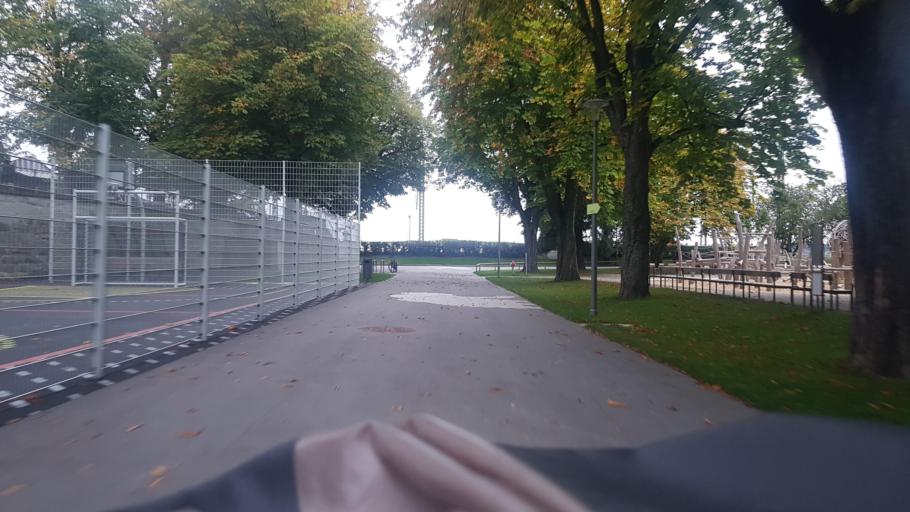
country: DE
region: Bavaria
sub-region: Swabia
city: Lindau
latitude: 47.5480
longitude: 9.6821
